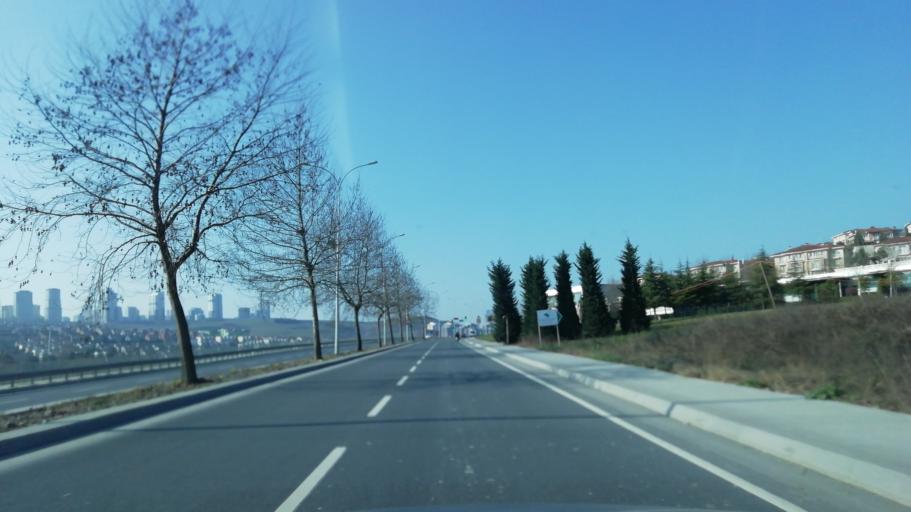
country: TR
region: Istanbul
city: Esenyurt
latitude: 41.0842
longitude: 28.6802
